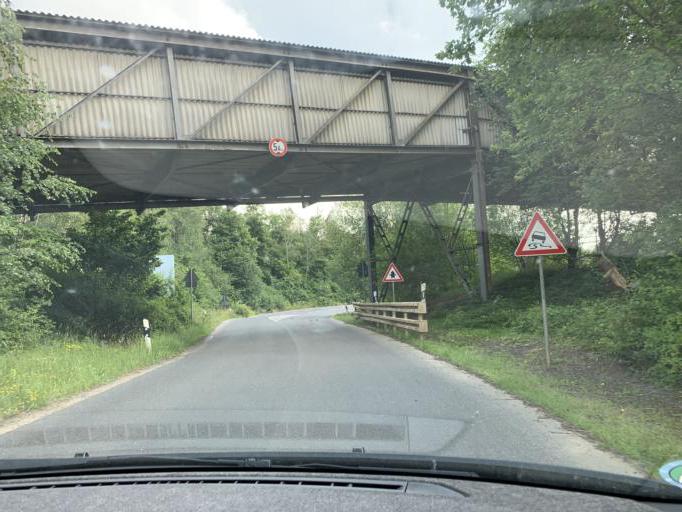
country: DE
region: North Rhine-Westphalia
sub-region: Regierungsbezirk Dusseldorf
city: Grevenbroich
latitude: 51.0461
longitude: 6.5650
